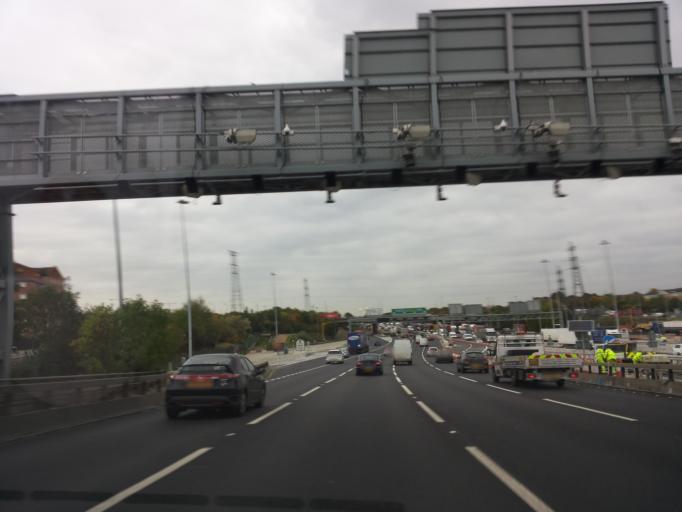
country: GB
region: England
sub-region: Kent
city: Stone
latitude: 51.4549
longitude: 0.2461
